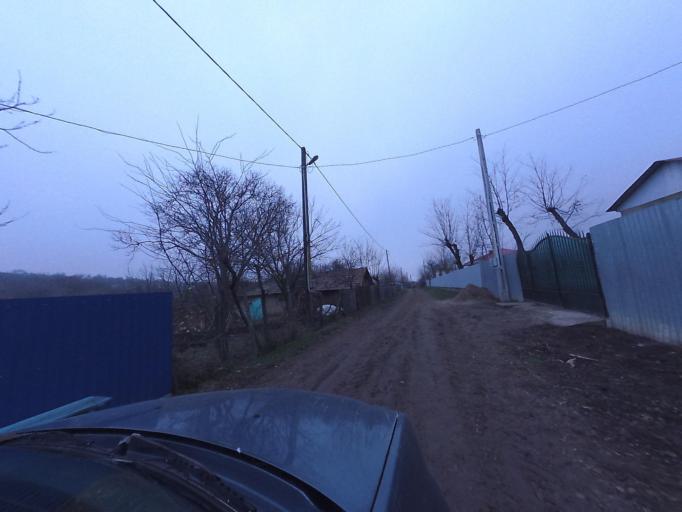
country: RO
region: Vaslui
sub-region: Comuna Vinderei
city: Vinderei
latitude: 46.1455
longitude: 27.7484
